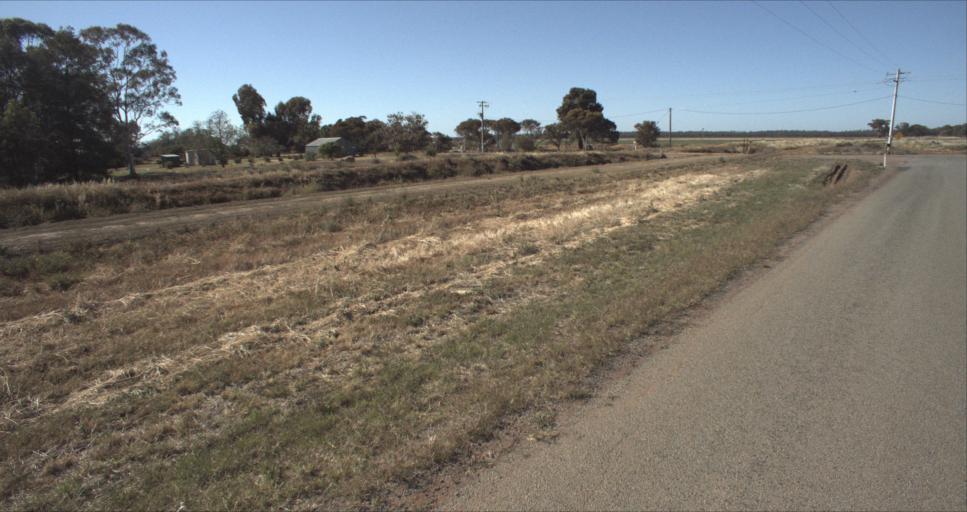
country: AU
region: New South Wales
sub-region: Leeton
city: Leeton
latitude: -34.5827
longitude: 146.3085
